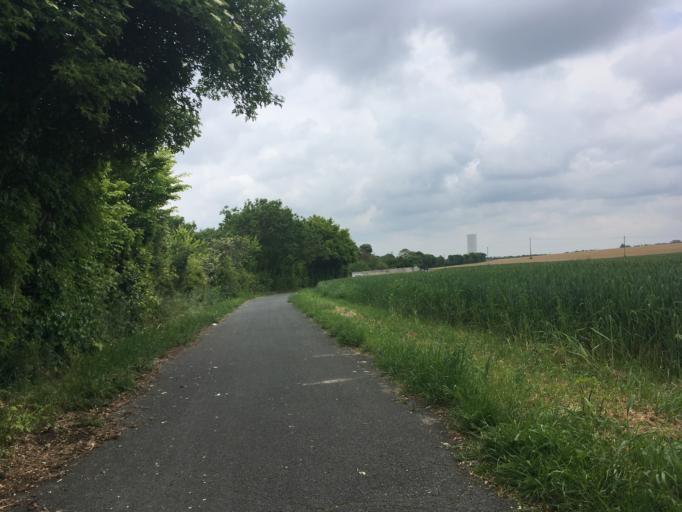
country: FR
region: Poitou-Charentes
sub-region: Departement de la Charente-Maritime
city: Aytre
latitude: 46.1464
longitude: -1.1241
